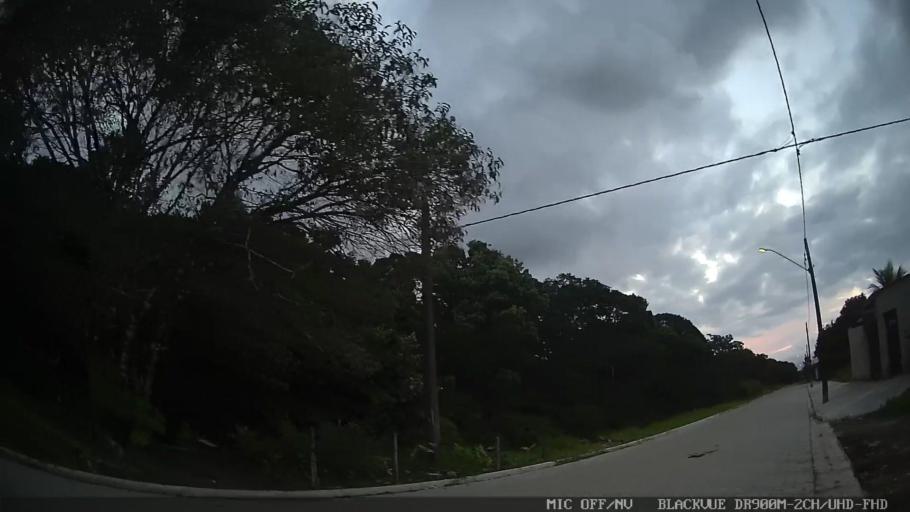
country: BR
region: Sao Paulo
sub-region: Itanhaem
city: Itanhaem
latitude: -24.1898
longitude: -46.8341
